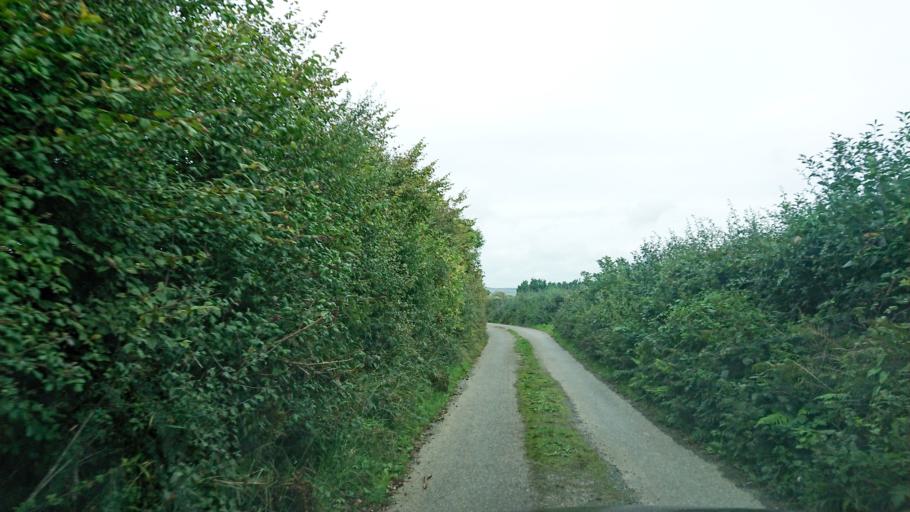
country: IE
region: Munster
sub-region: Waterford
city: Dunmore East
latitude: 52.2069
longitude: -7.0438
